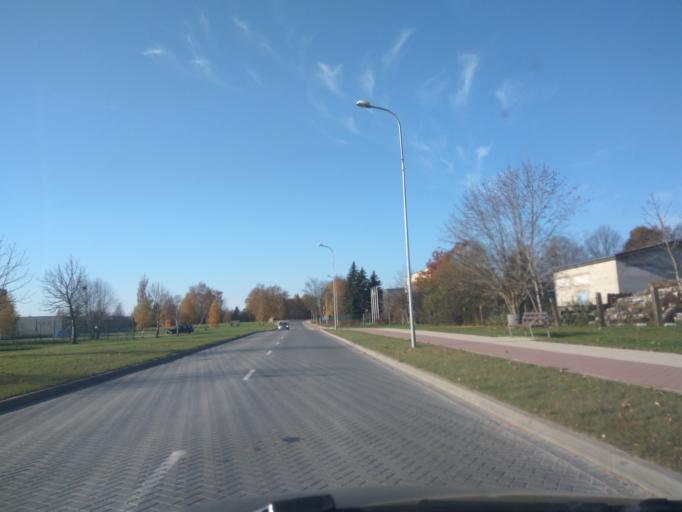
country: LV
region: Kuldigas Rajons
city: Kuldiga
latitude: 56.9804
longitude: 21.9461
